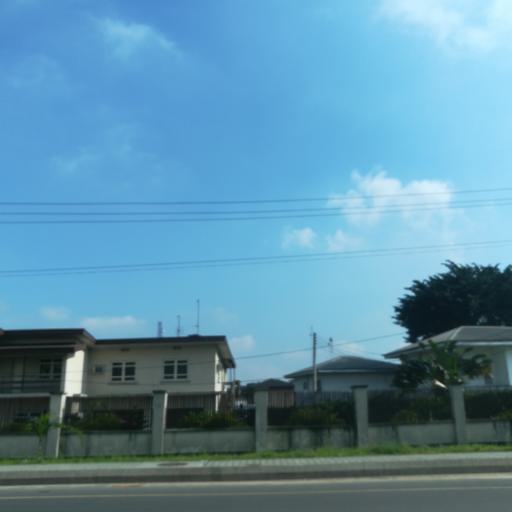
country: NG
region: Rivers
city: Port Harcourt
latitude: 4.8073
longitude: 7.0216
